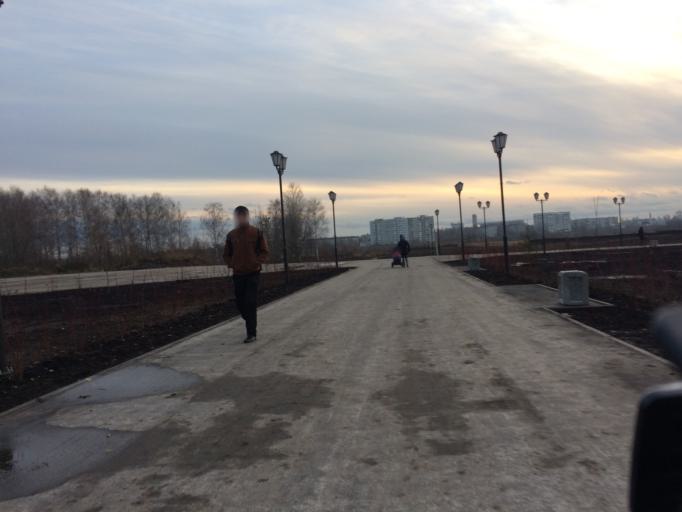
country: RU
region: Mariy-El
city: Yoshkar-Ola
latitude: 56.6266
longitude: 47.9081
